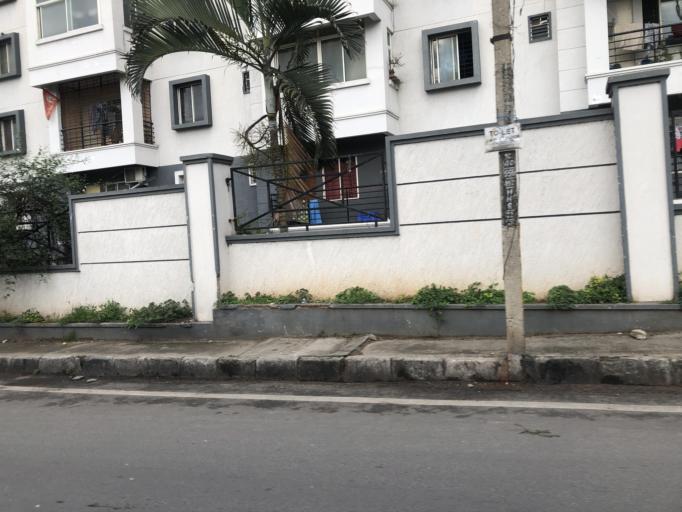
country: IN
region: Karnataka
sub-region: Bangalore Urban
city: Bangalore
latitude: 12.9483
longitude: 77.5388
